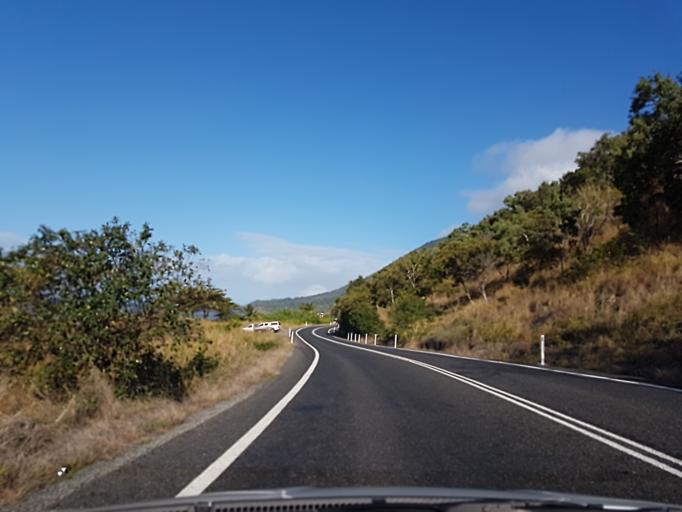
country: AU
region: Queensland
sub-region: Cairns
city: Palm Cove
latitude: -16.7136
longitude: 145.6354
